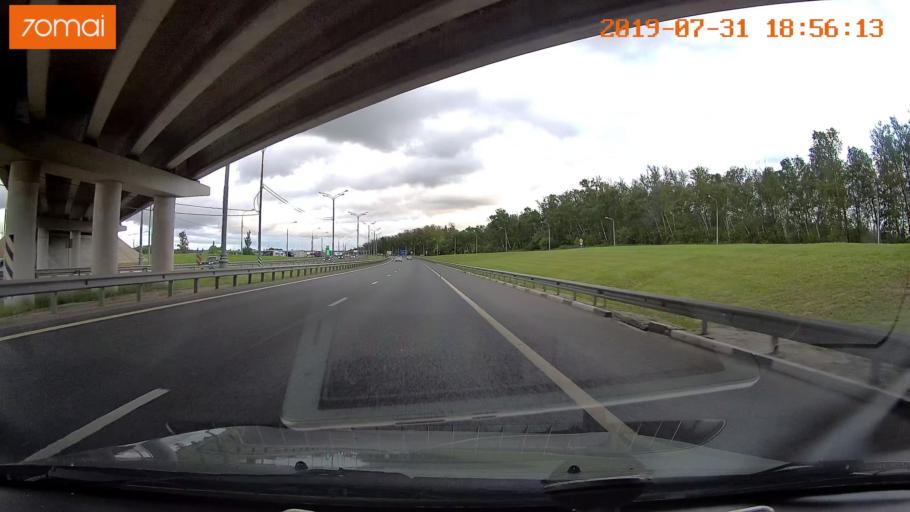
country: RU
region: Moskovskaya
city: Raduzhnyy
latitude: 55.1656
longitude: 38.6747
